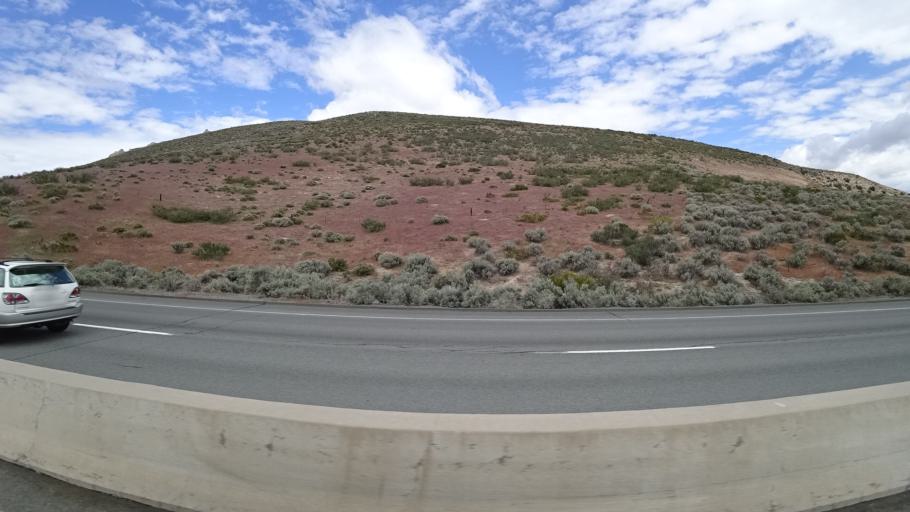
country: US
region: Nevada
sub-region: Douglas County
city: Indian Hills
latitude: 39.1147
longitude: -119.7834
